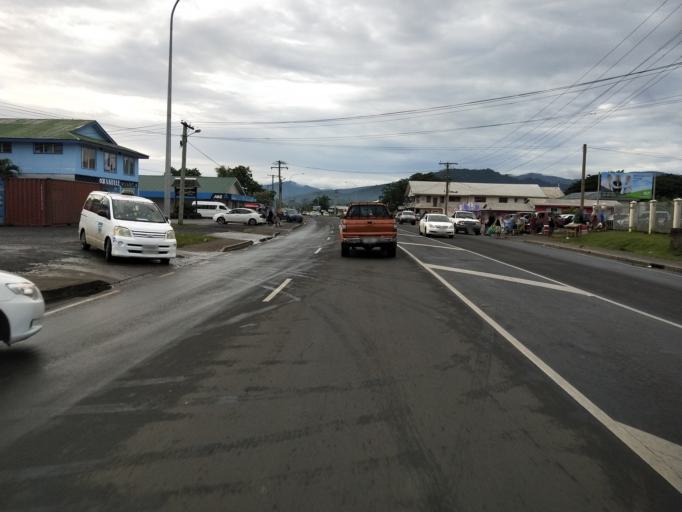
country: WS
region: Tuamasaga
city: Vaiusu
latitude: -13.8189
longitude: -171.8061
